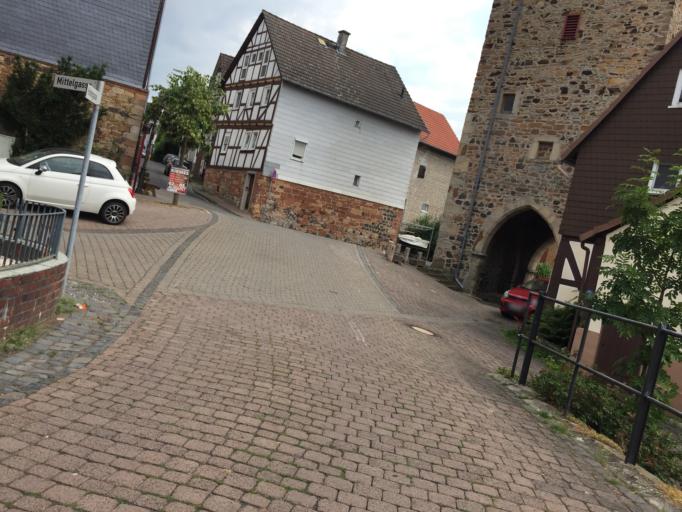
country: DE
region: Hesse
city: Staufenberg
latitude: 50.6638
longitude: 8.7269
